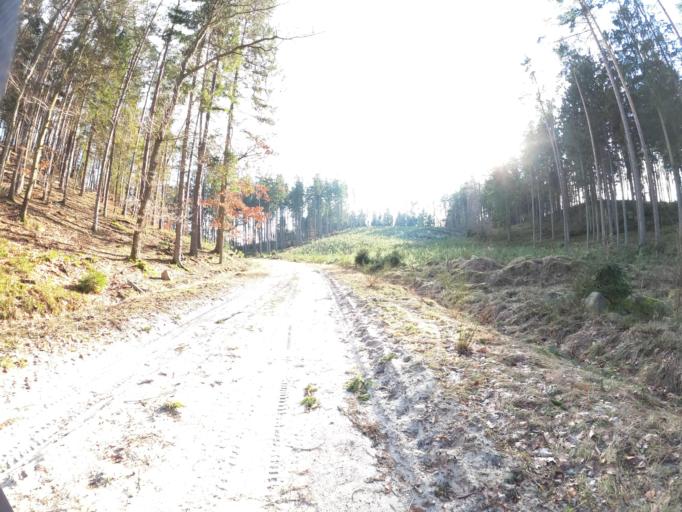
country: PL
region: West Pomeranian Voivodeship
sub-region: Powiat koszalinski
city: Polanow
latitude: 54.2179
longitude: 16.6410
